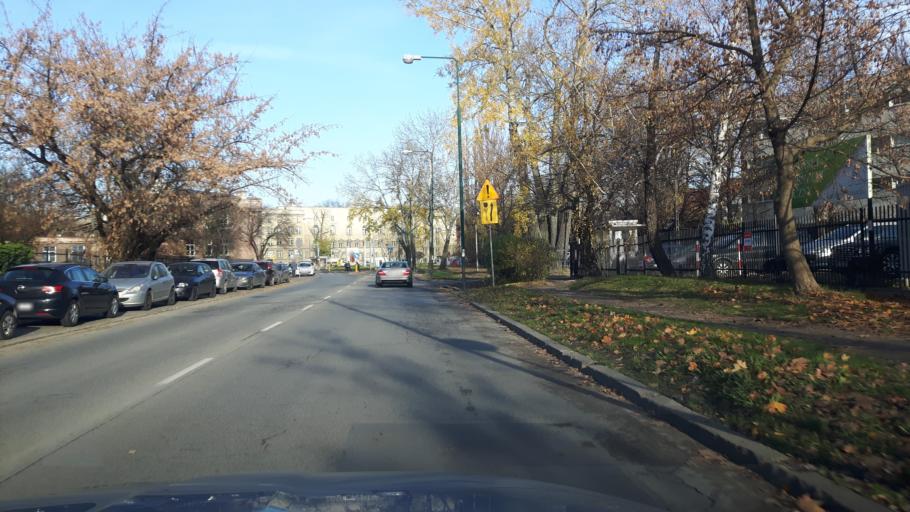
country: PL
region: Masovian Voivodeship
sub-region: Warszawa
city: Ochota
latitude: 52.2087
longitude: 20.9797
